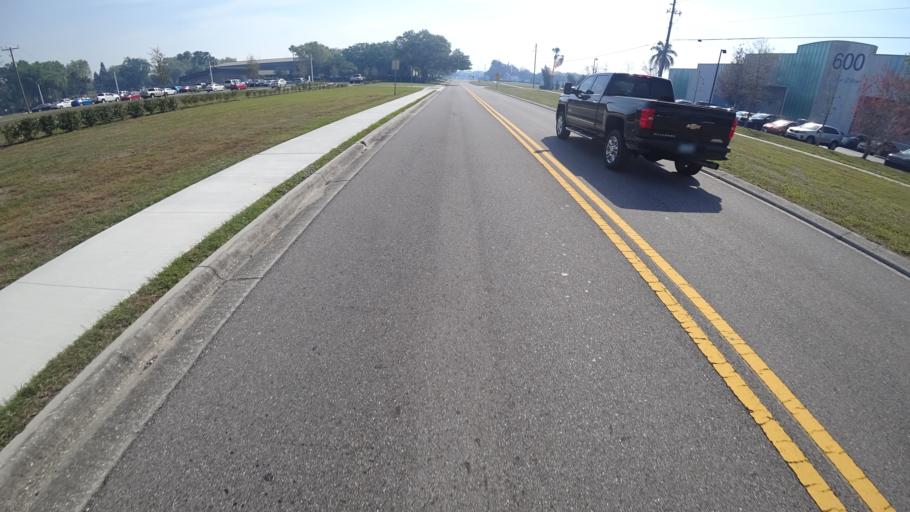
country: US
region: Florida
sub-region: Manatee County
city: Whitfield
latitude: 27.4077
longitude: -82.5621
